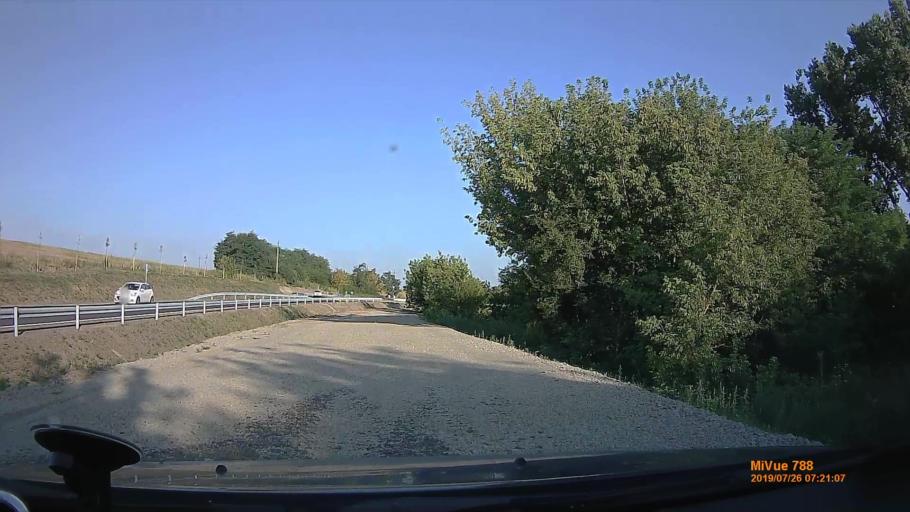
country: HU
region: Pest
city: Mogyorod
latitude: 47.5961
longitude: 19.2215
